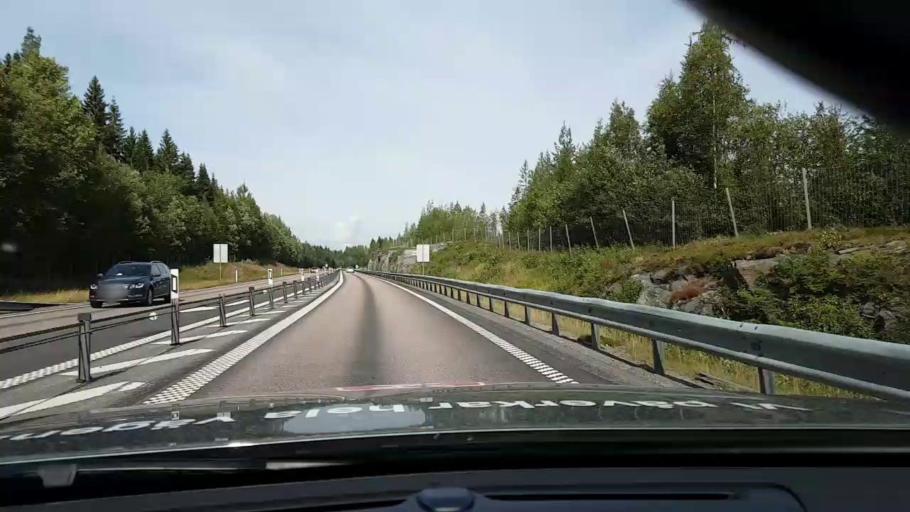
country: SE
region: Vaesternorrland
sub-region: OErnskoeldsviks Kommun
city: Husum
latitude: 63.4327
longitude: 19.2103
